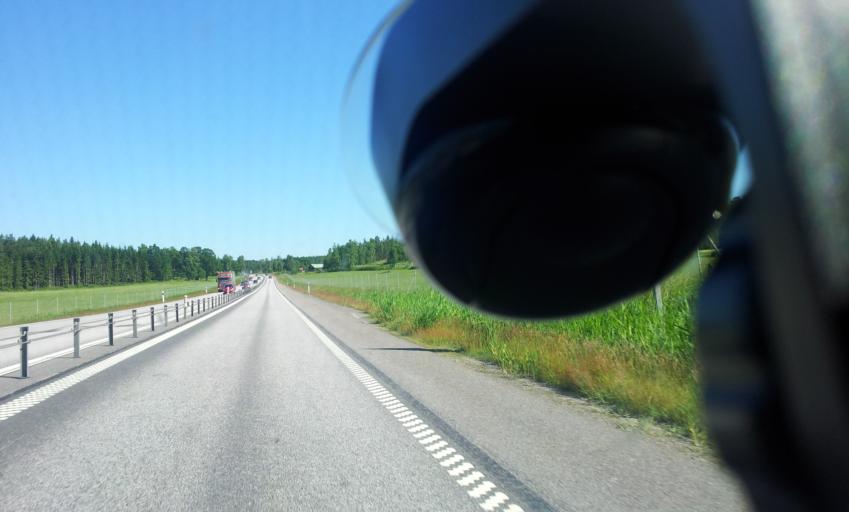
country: SE
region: OEstergoetland
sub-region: Soderkopings Kommun
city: Soederkoeping
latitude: 58.4040
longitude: 16.4023
